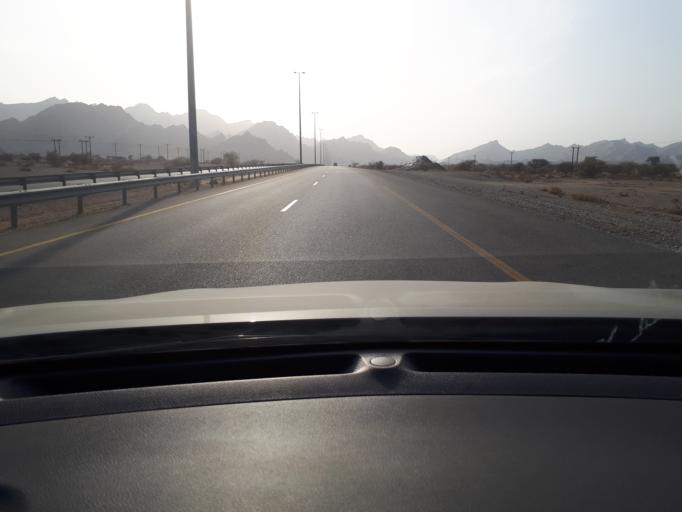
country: OM
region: Muhafazat Masqat
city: Muscat
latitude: 23.3631
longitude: 58.6637
